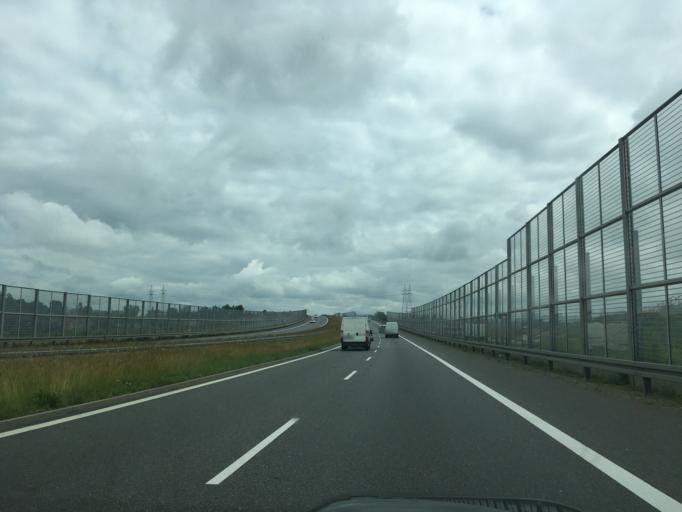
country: PL
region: Lublin Voivodeship
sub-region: Powiat lubelski
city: Jakubowice Murowane
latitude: 51.2894
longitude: 22.6153
